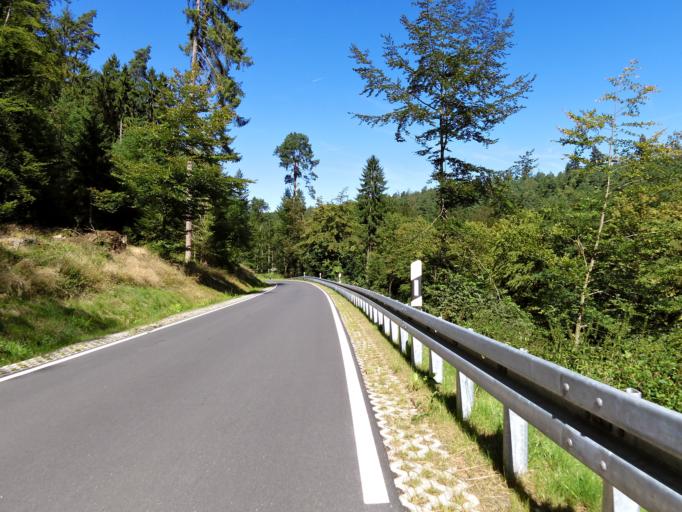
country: DE
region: Hesse
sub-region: Regierungsbezirk Darmstadt
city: Erbach
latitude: 49.6586
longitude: 8.9680
